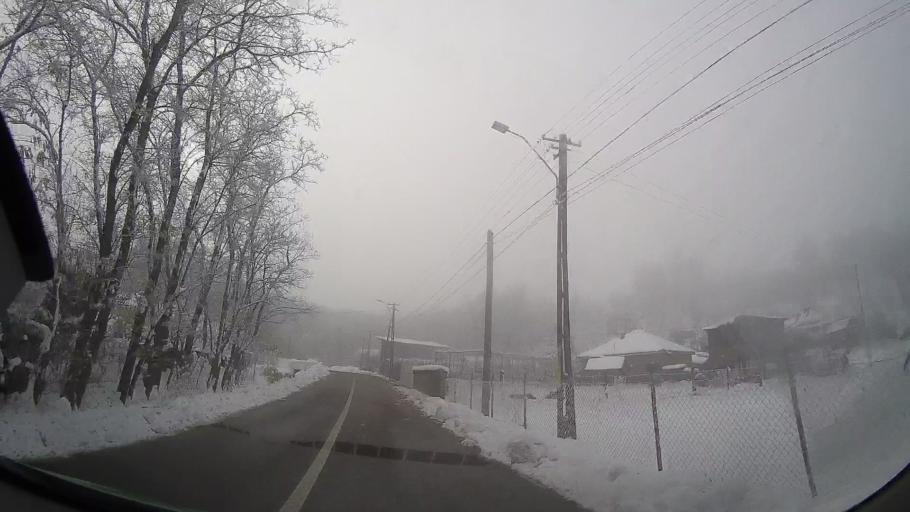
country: RO
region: Iasi
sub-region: Comuna Valea Seaca
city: Valea Seaca
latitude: 47.2870
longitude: 26.6686
